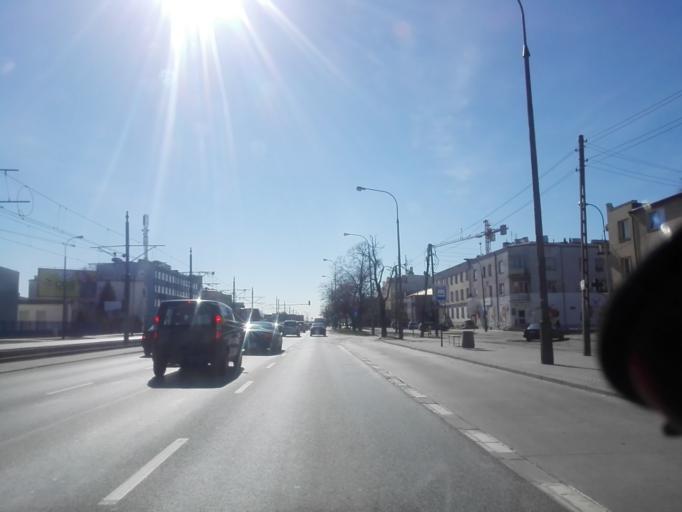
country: PL
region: Masovian Voivodeship
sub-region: Warszawa
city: Wlochy
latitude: 52.1806
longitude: 20.9483
